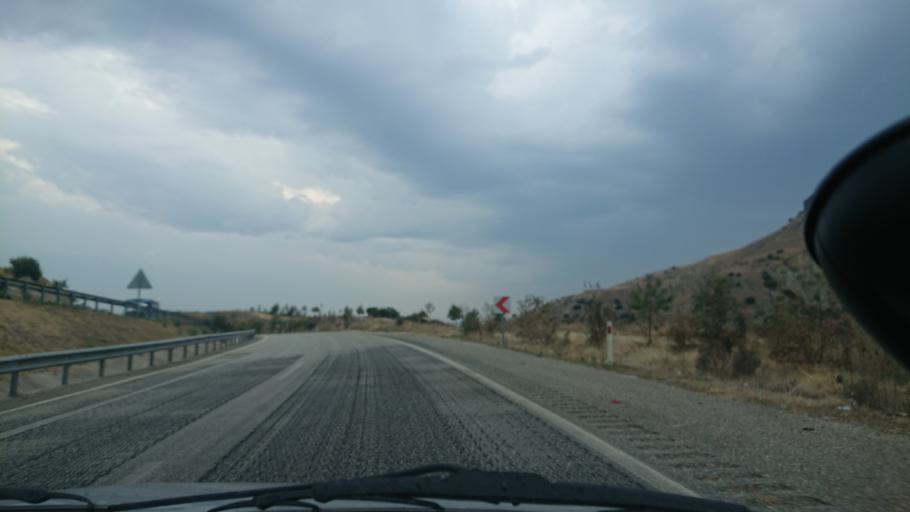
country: TR
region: Manisa
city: Selendi
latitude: 38.6016
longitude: 28.8141
